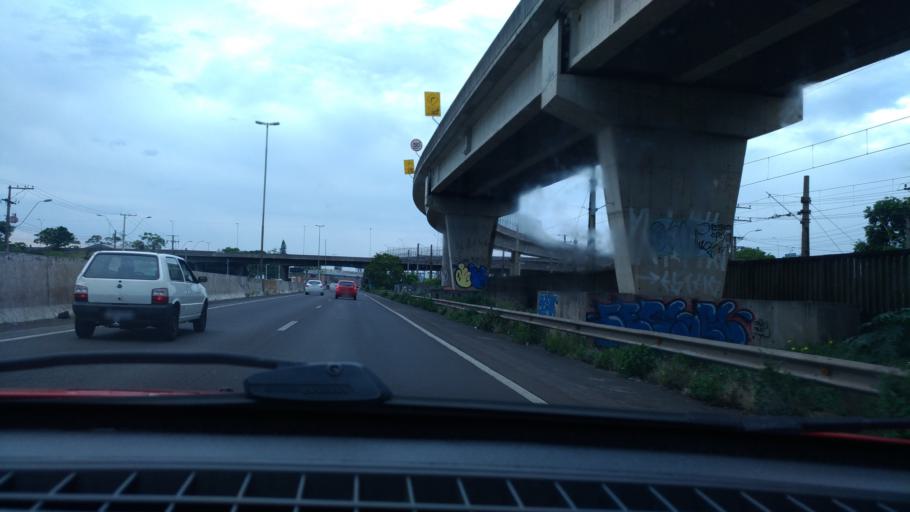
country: BR
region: Rio Grande do Sul
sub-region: Canoas
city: Canoas
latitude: -29.8909
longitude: -51.1780
